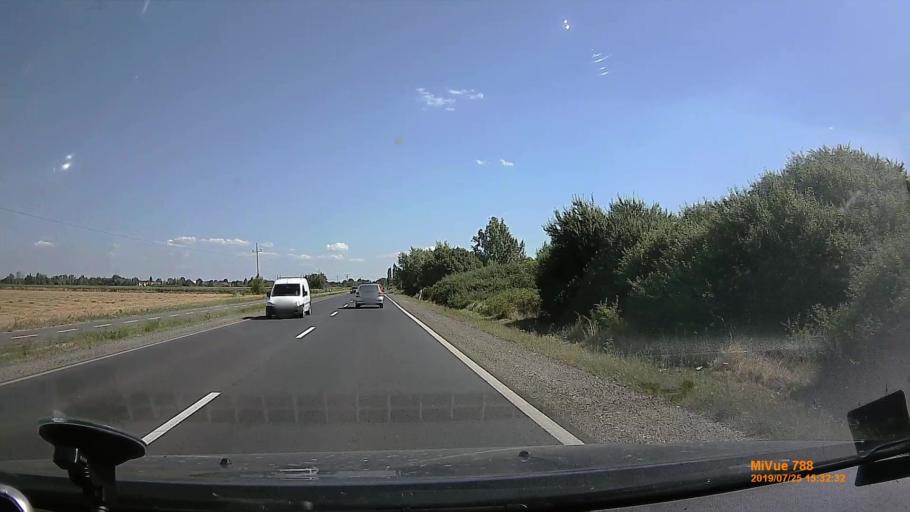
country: HU
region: Borsod-Abauj-Zemplen
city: Malyi
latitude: 48.0055
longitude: 20.8289
